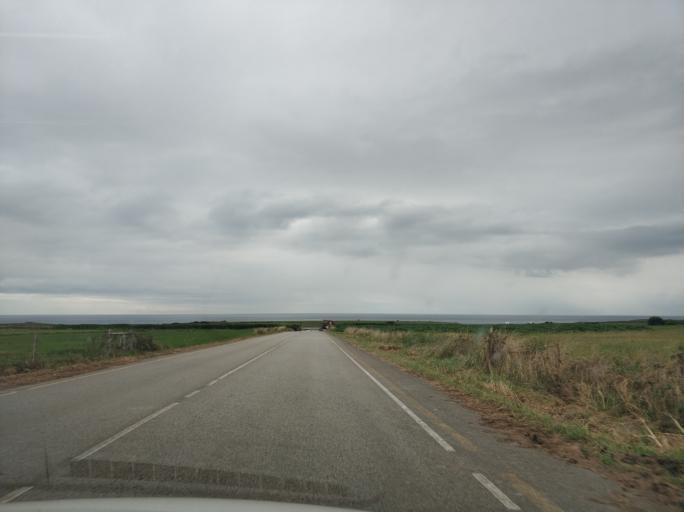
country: ES
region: Galicia
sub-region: Provincia de Lugo
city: Barreiros
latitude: 43.5491
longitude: -7.1518
